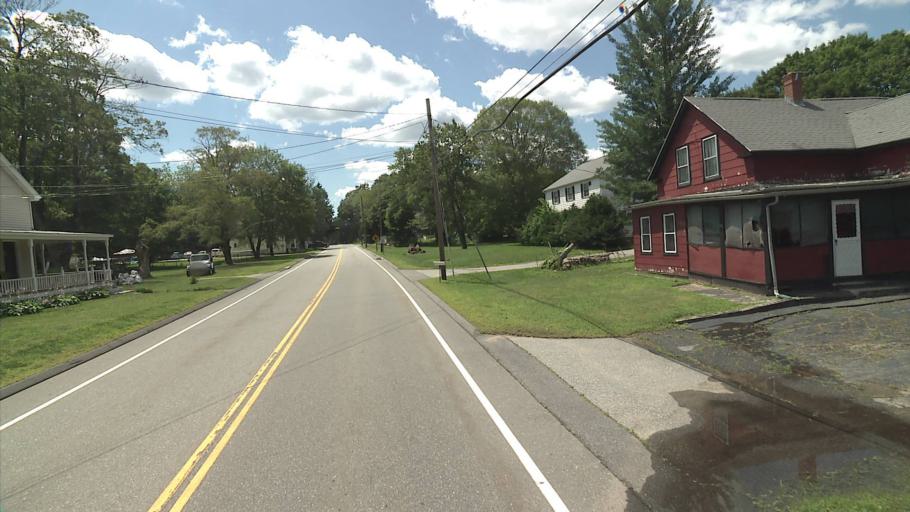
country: US
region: Connecticut
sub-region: Windham County
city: Quinebaug
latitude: 42.0256
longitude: -71.9448
